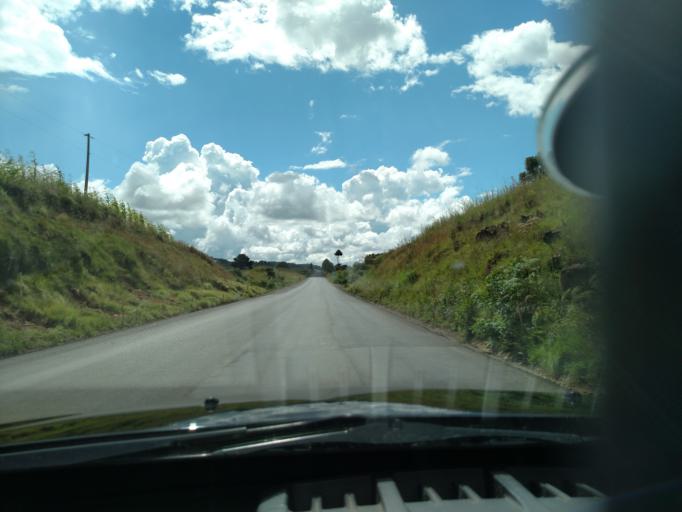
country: BR
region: Santa Catarina
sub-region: Lages
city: Lages
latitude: -27.9210
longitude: -50.1065
